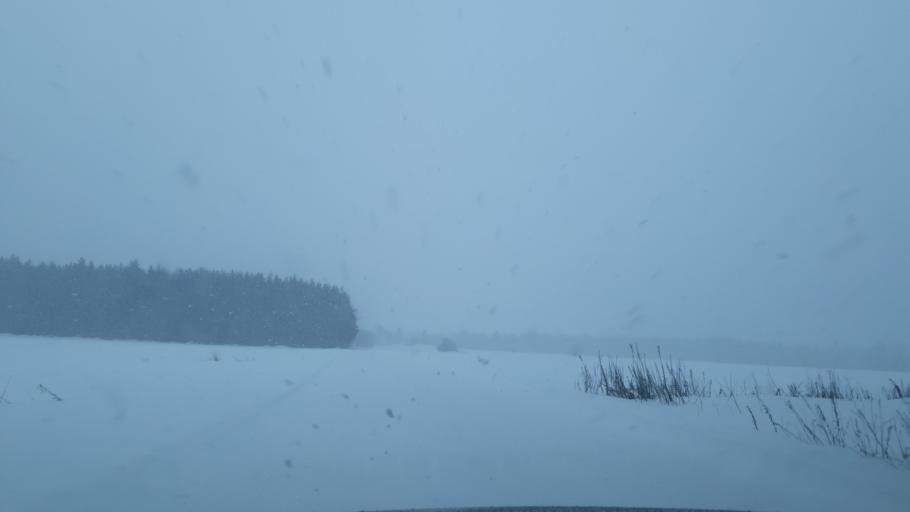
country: EE
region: Jaervamaa
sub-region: Jaerva-Jaani vald
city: Jarva-Jaani
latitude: 59.0819
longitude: 25.7813
